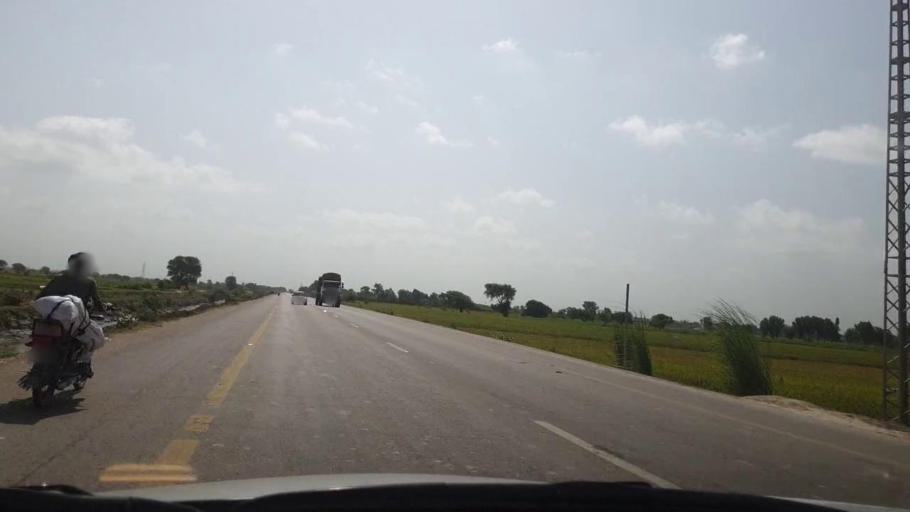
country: PK
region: Sindh
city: Matli
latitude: 24.9756
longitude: 68.6728
